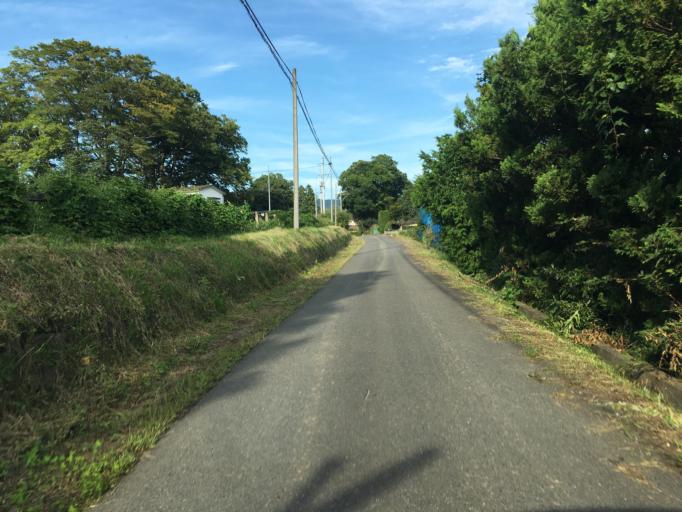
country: JP
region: Fukushima
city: Hobaramachi
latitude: 37.8738
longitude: 140.5184
